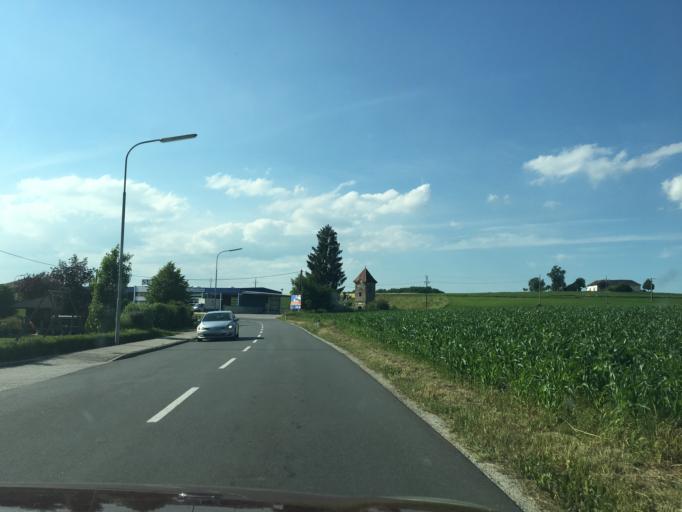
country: AT
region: Lower Austria
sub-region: Politischer Bezirk Amstetten
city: Ennsdorf
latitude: 48.2735
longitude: 14.5220
